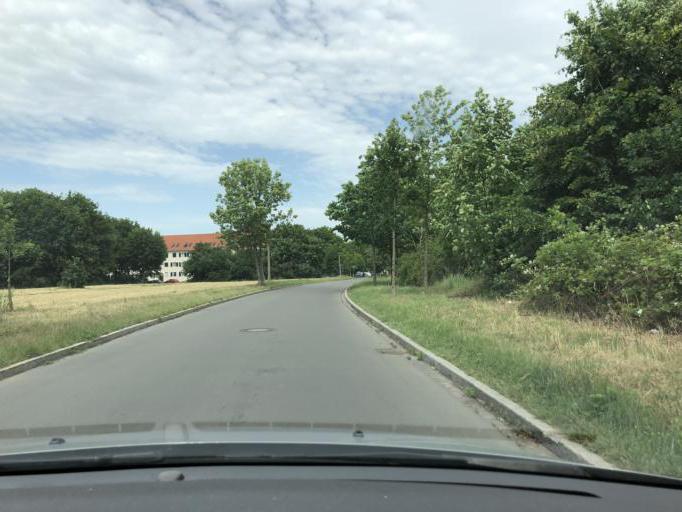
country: DE
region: Saxony
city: Taucha
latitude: 51.3836
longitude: 12.4865
